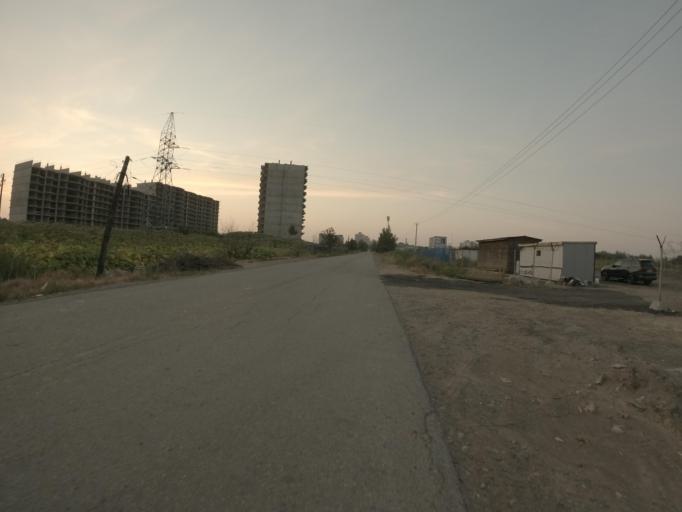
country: RU
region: Leningrad
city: Yanino Vtoroye
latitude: 59.9417
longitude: 30.5530
